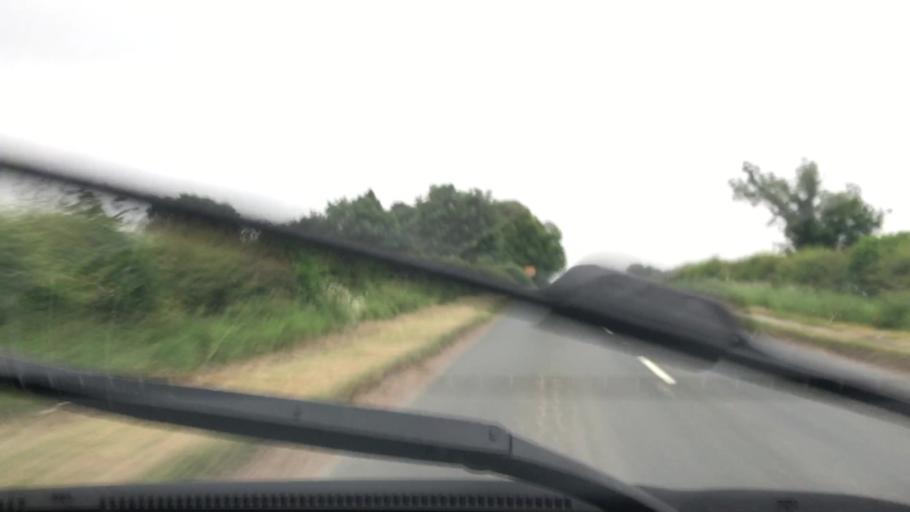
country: GB
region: England
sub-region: City and Borough of Leeds
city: Wetherby
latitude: 53.9543
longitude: -1.3995
